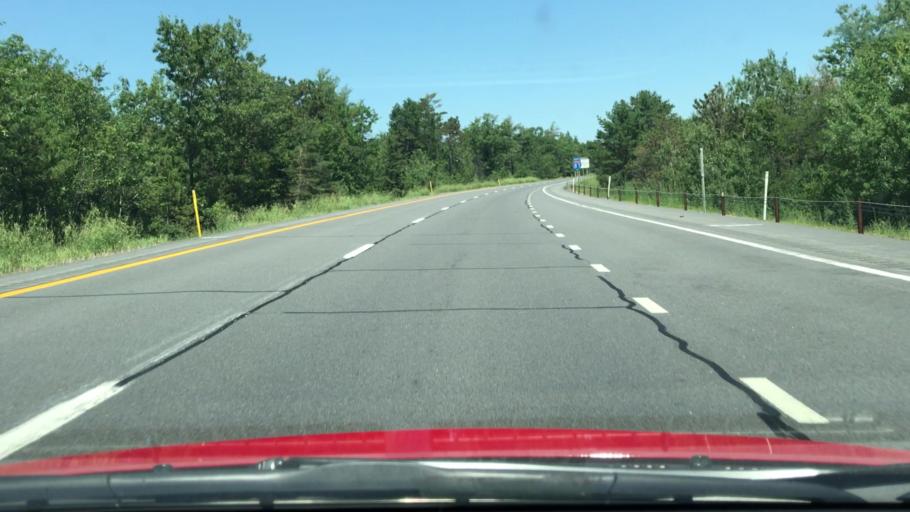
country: US
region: New York
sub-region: Essex County
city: Keeseville
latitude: 44.4984
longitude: -73.5010
